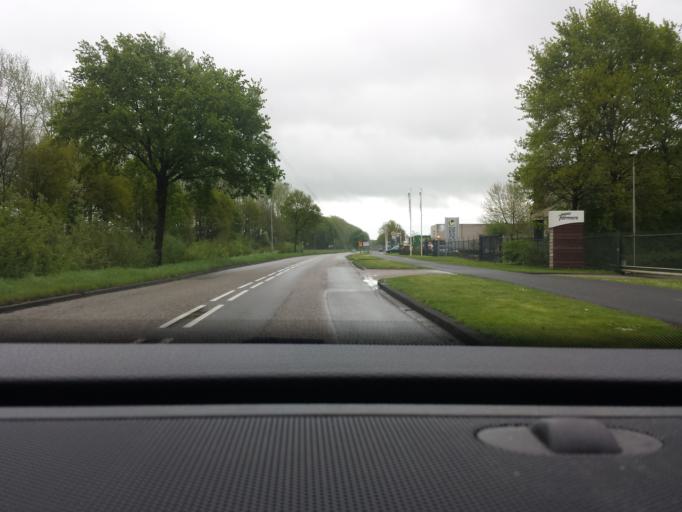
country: NL
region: Gelderland
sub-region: Gemeente Lochem
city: Lochem
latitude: 52.1690
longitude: 6.4052
